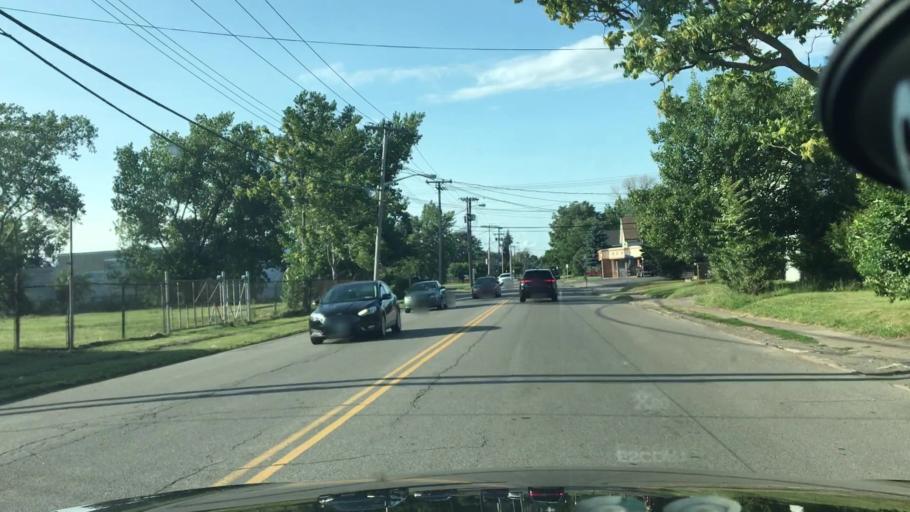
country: US
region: New York
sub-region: Erie County
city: Lackawanna
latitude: 42.8479
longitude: -78.8323
